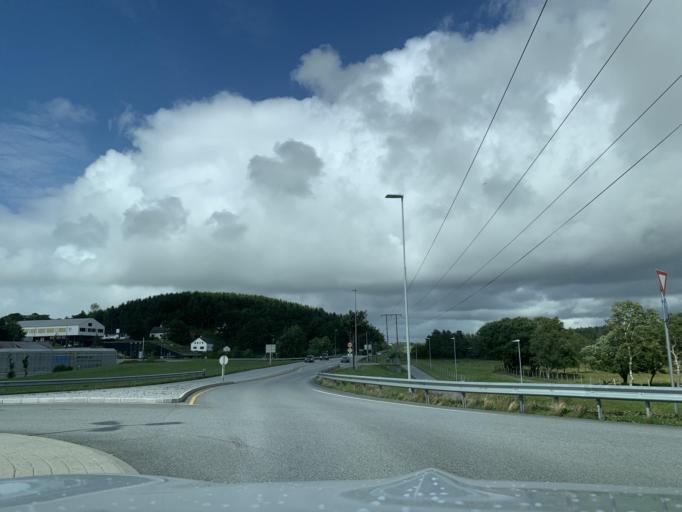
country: NO
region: Rogaland
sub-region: Klepp
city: Kleppe
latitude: 58.7979
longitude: 5.6718
